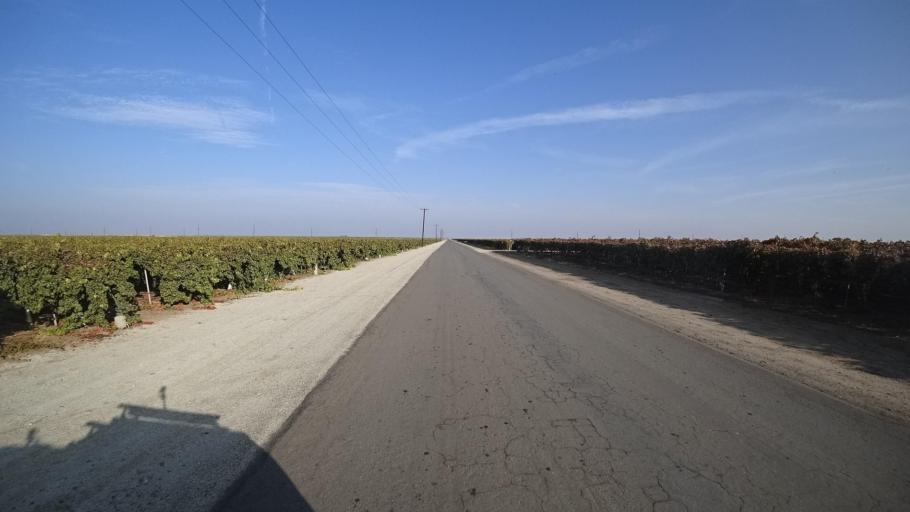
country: US
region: California
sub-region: Kern County
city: McFarland
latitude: 35.6993
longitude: -119.1871
